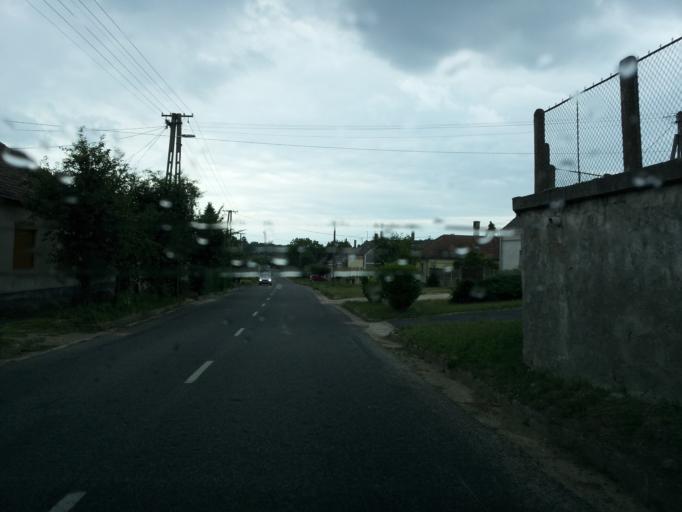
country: HU
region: Zala
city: Turje
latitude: 47.0921
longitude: 17.0227
